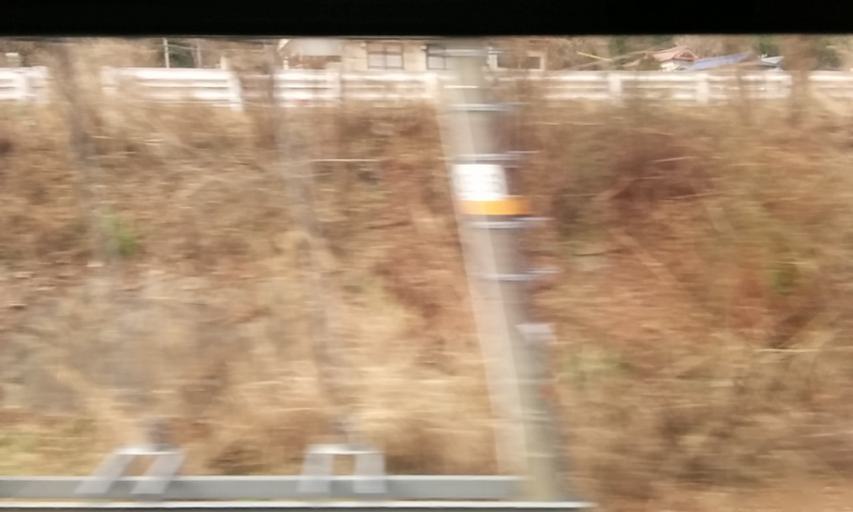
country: JP
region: Nagano
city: Shiojiri
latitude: 36.0234
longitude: 137.8699
